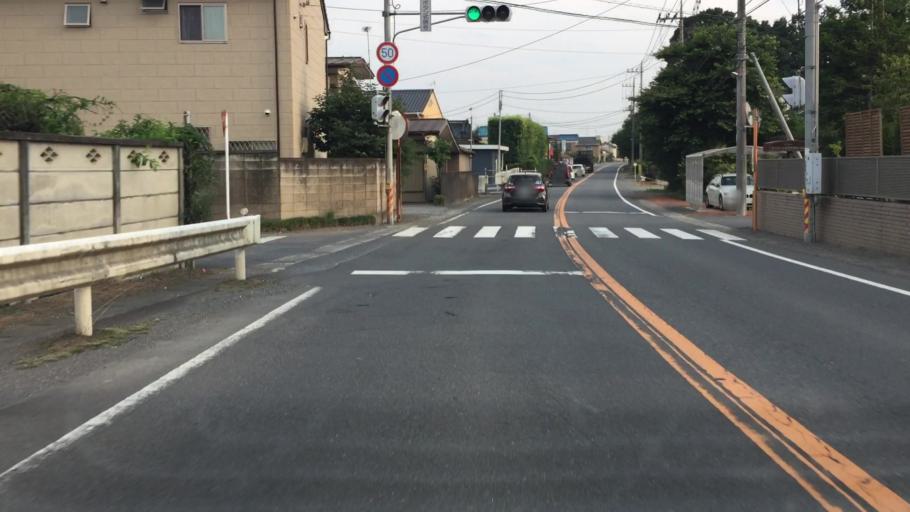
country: JP
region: Tochigi
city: Fujioka
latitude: 36.2881
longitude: 139.6667
